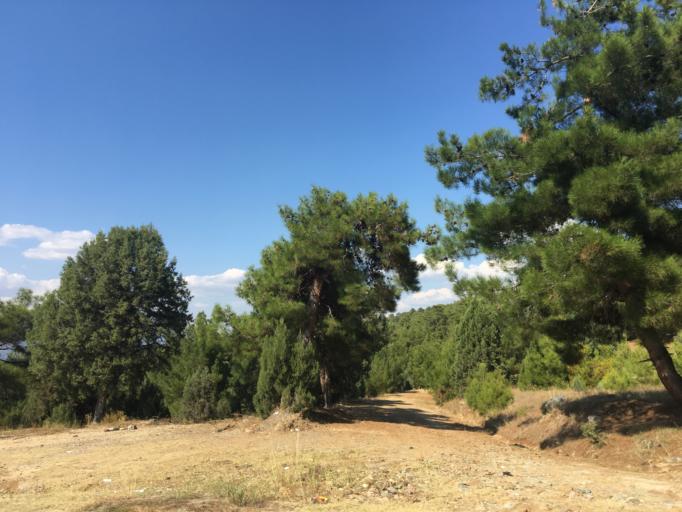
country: TR
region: Ankara
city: Beydili
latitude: 40.0642
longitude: 30.9233
